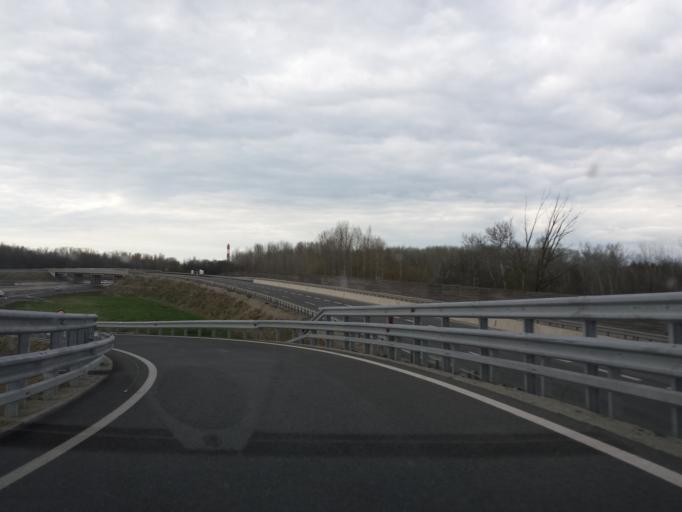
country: AT
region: Lower Austria
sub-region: Politischer Bezirk Sankt Polten
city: Traismauer
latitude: 48.3725
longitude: 15.7158
